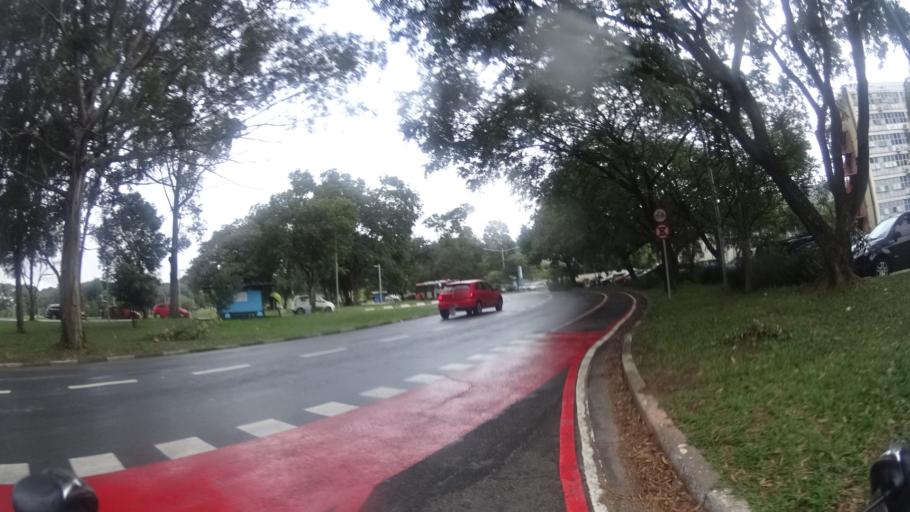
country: BR
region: Sao Paulo
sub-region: Osasco
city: Osasco
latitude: -23.5611
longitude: -46.7211
